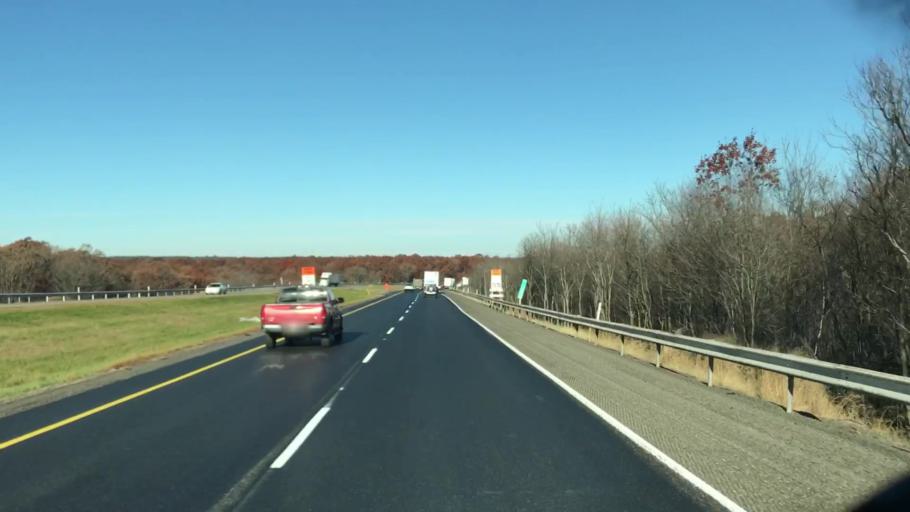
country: US
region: Pennsylvania
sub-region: Schuylkill County
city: McAdoo
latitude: 40.8914
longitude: -76.0233
